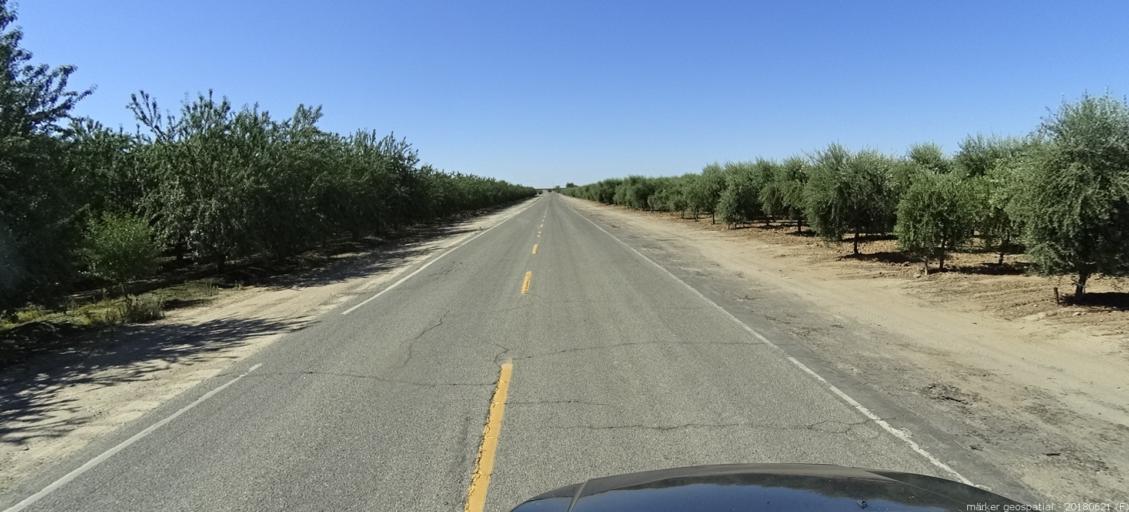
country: US
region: California
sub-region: Fresno County
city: Biola
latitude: 36.8628
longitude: -119.9471
